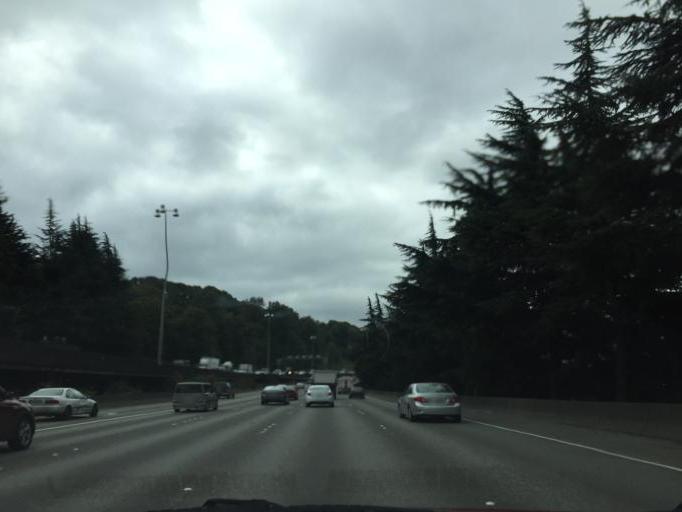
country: US
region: Washington
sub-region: King County
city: Seattle
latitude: 47.5819
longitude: -122.3198
